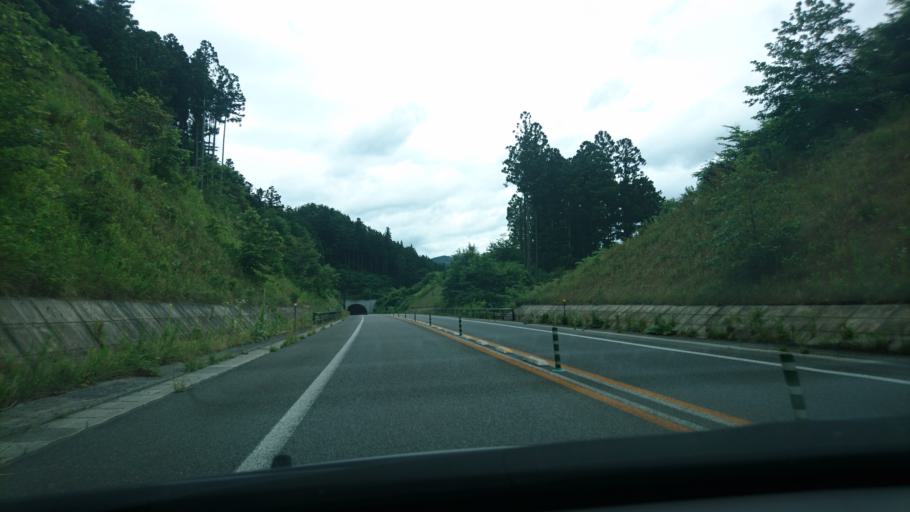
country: JP
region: Iwate
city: Kamaishi
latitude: 39.3155
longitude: 141.8836
